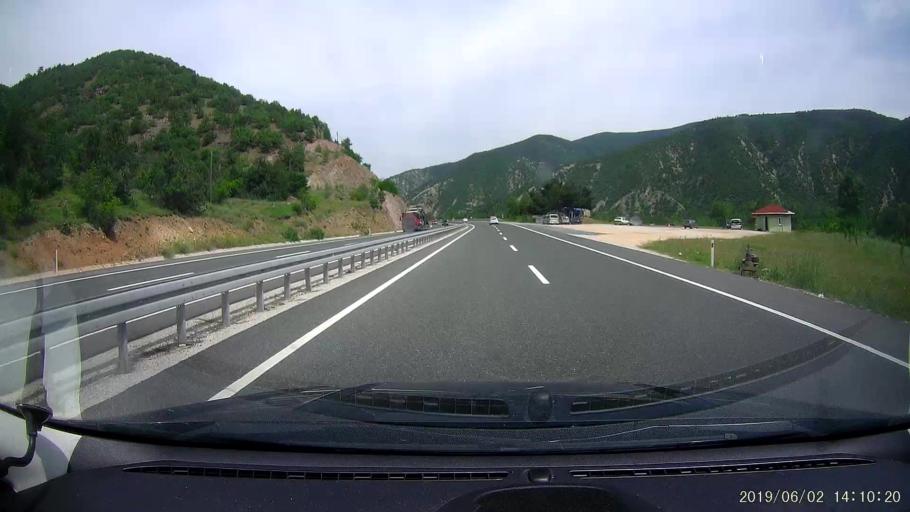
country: TR
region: Cankiri
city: Ilgaz
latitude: 40.9033
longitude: 33.7579
